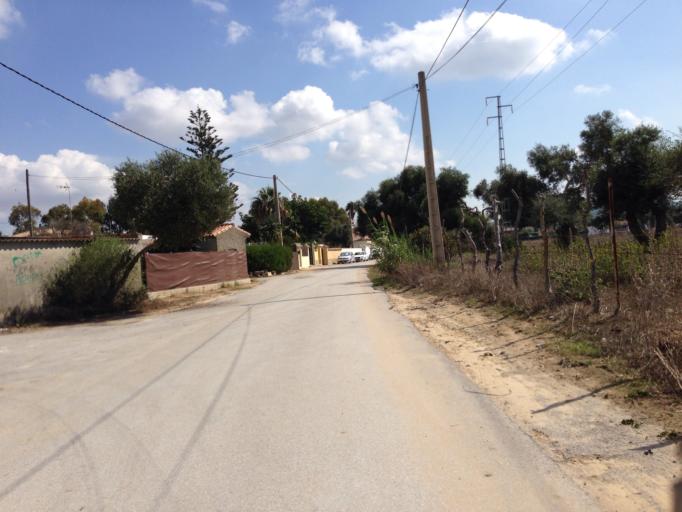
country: ES
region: Andalusia
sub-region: Provincia de Cadiz
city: Vejer de la Frontera
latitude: 36.2077
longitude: -6.0418
